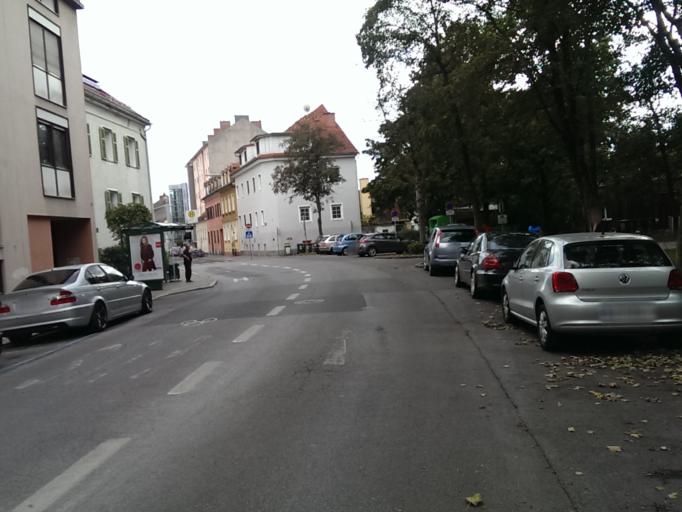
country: AT
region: Styria
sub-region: Graz Stadt
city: Graz
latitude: 47.0603
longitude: 15.4367
